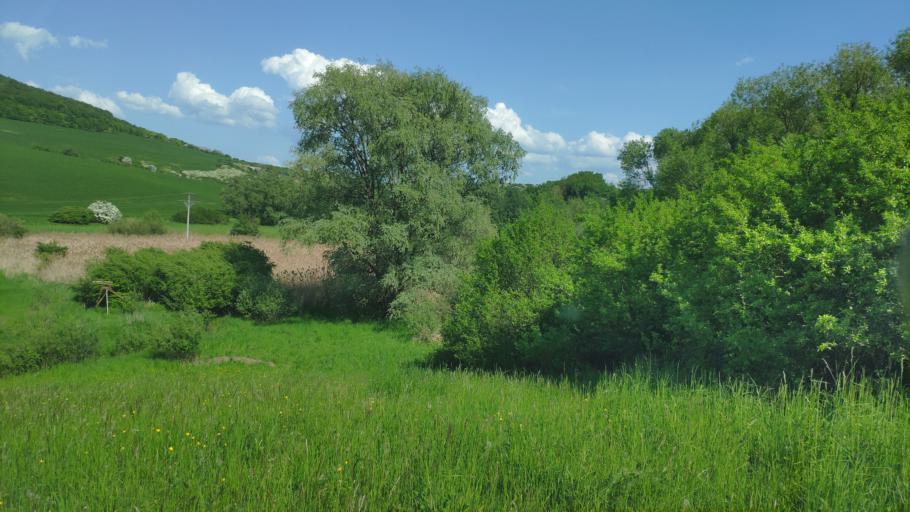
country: SK
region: Presovsky
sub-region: Okres Presov
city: Presov
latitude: 49.0453
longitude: 21.1630
